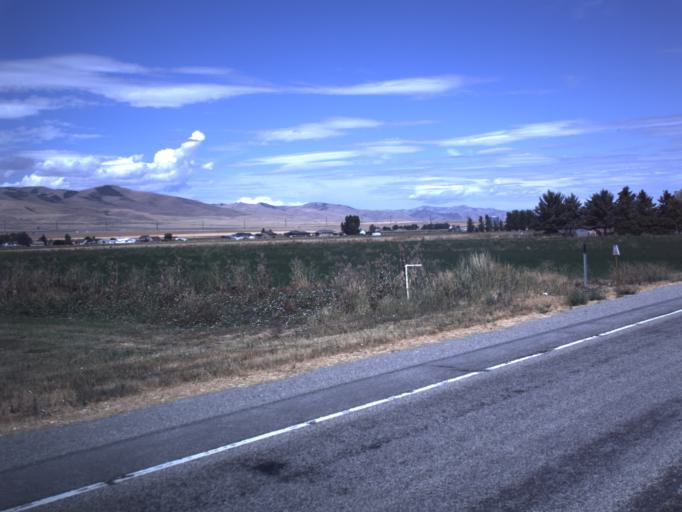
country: US
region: Utah
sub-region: Box Elder County
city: Garland
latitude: 41.8075
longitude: -112.1450
